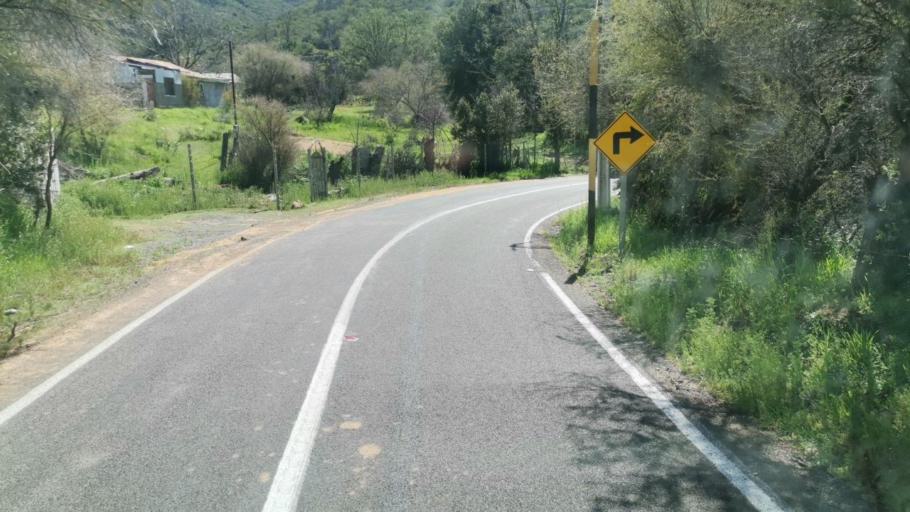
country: CL
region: Valparaiso
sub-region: Provincia de Marga Marga
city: Limache
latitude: -33.1802
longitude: -71.1854
